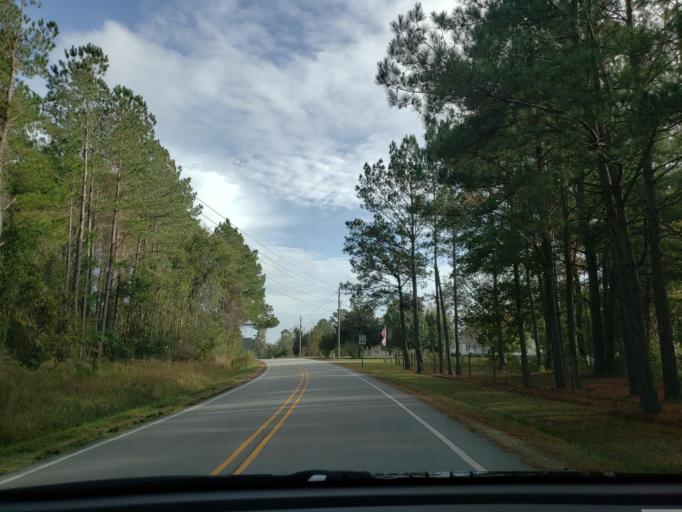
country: US
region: North Carolina
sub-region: Onslow County
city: Jacksonville
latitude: 34.6714
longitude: -77.4989
